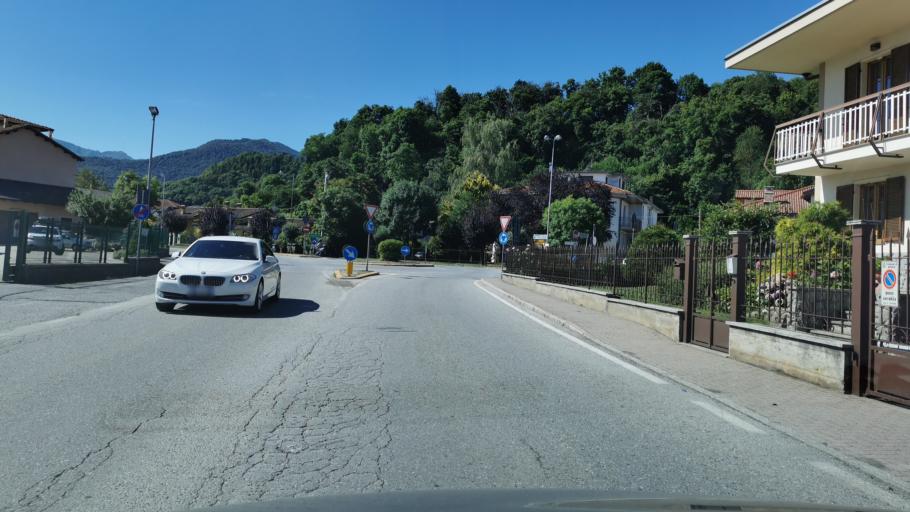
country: IT
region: Piedmont
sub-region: Provincia di Cuneo
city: Boves
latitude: 44.3357
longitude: 7.5444
